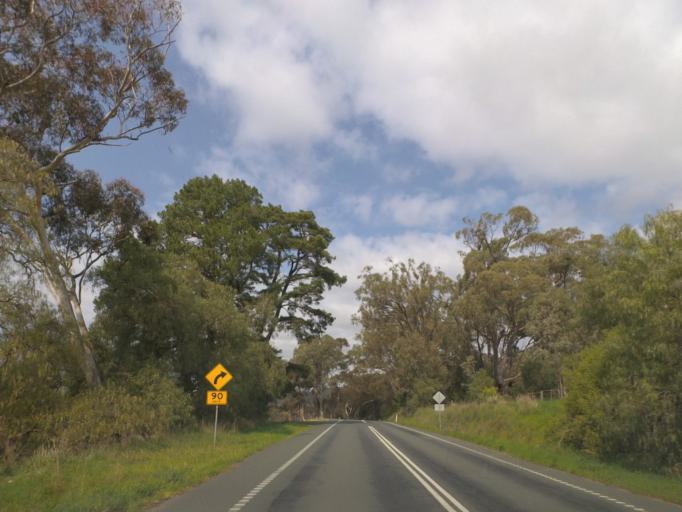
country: AU
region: Victoria
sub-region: Murrindindi
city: Kinglake West
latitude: -37.0978
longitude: 145.2079
